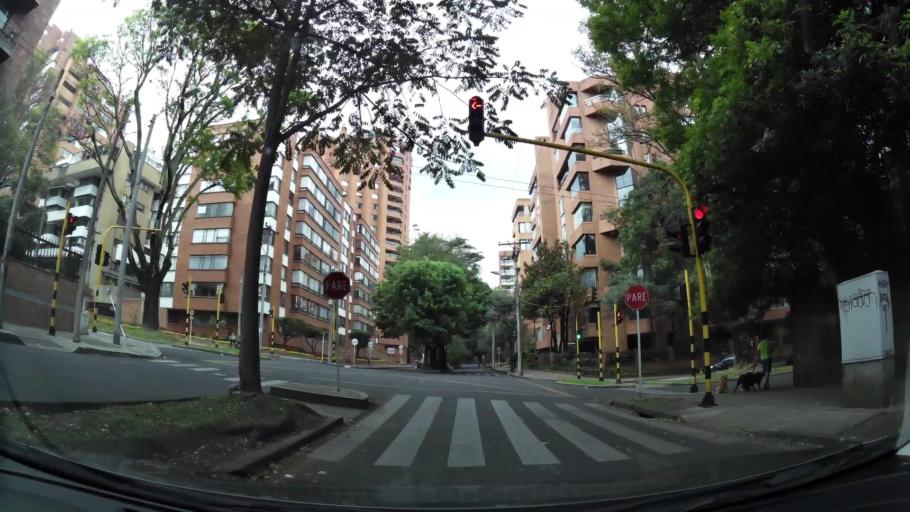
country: CO
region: Bogota D.C.
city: Barrio San Luis
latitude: 4.6678
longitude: -74.0485
